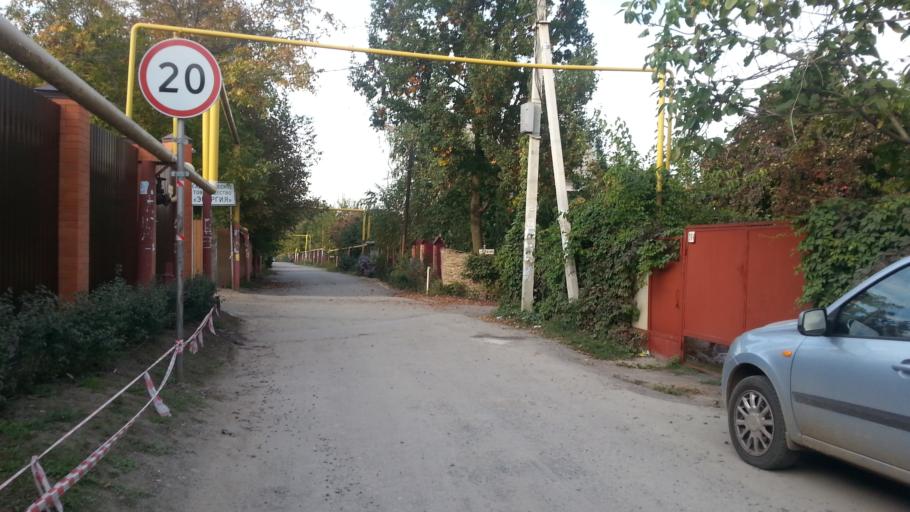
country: RU
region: Rostov
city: Severnyy
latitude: 47.2893
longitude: 39.6702
